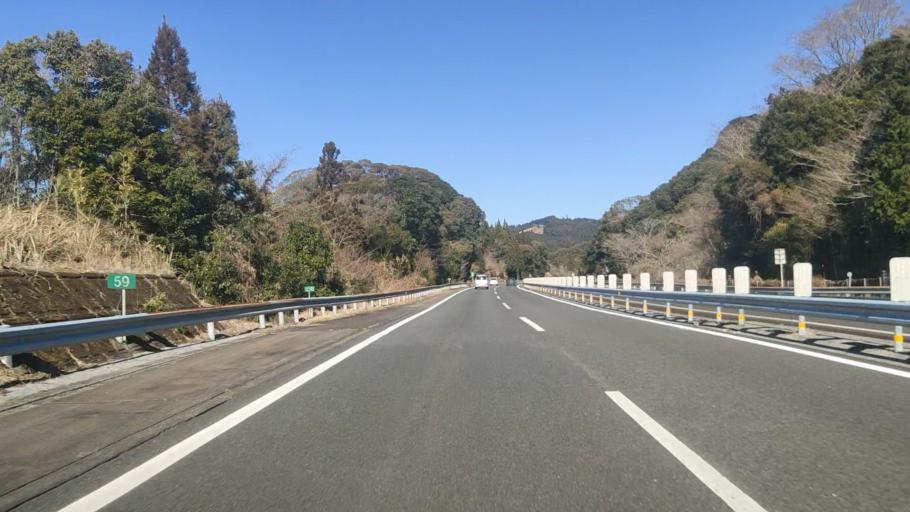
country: JP
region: Miyazaki
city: Miyakonojo
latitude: 31.8153
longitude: 131.2159
